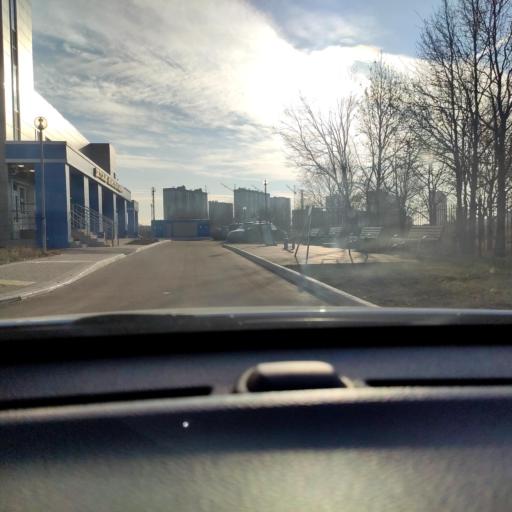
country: RU
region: Voronezj
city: Shilovo
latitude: 51.5720
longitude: 39.1179
